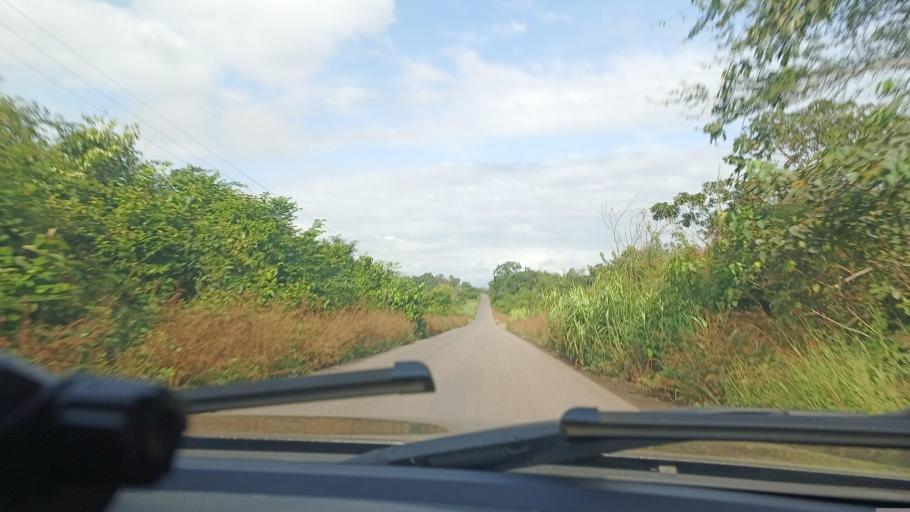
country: LR
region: Bomi
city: Tubmanburg
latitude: 6.6946
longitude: -10.8991
